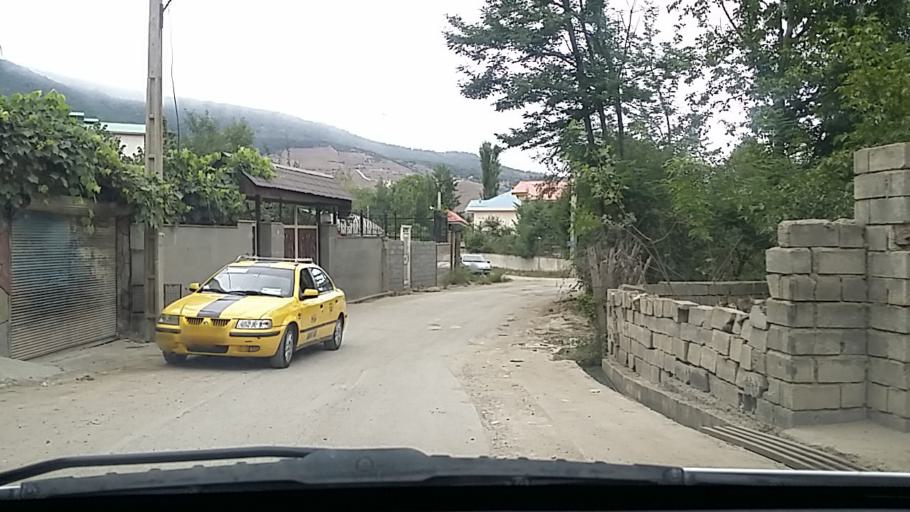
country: IR
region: Mazandaran
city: `Abbasabad
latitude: 36.5129
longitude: 51.1631
